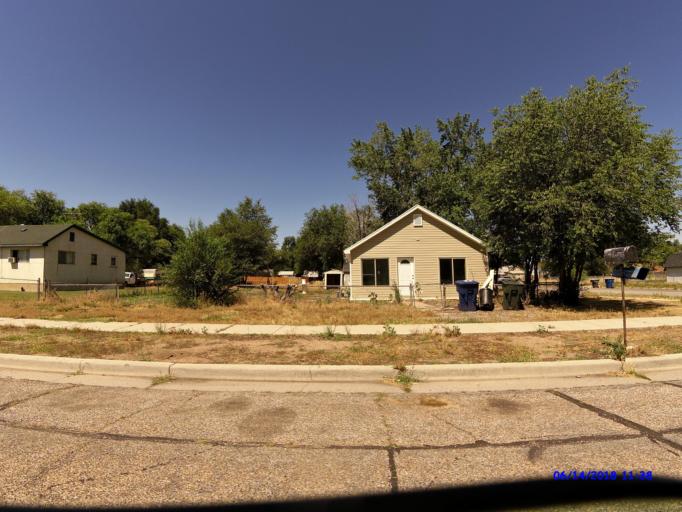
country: US
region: Utah
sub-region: Weber County
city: Ogden
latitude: 41.2208
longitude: -111.9900
